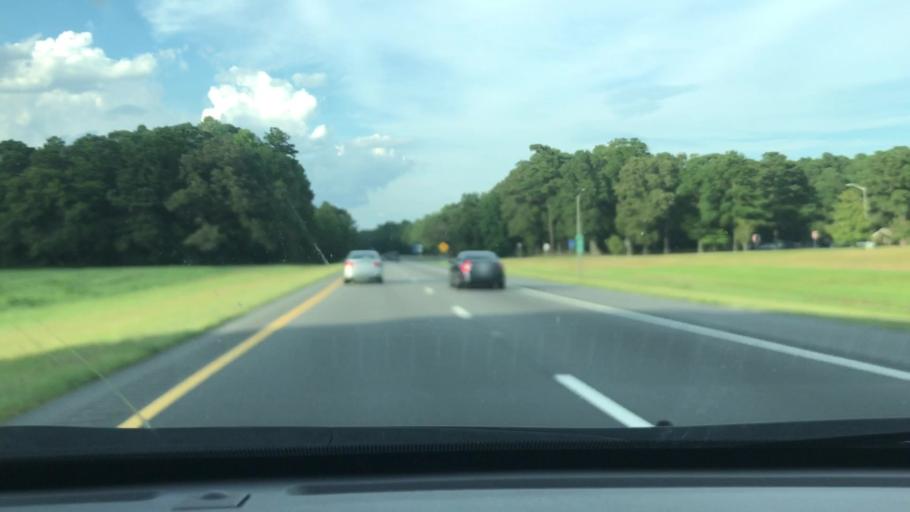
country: US
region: North Carolina
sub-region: Cumberland County
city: Vander
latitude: 34.9961
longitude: -78.8303
